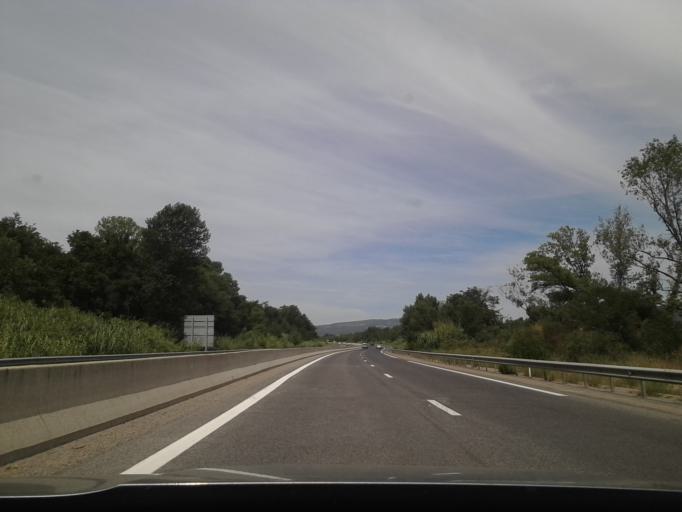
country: FR
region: Languedoc-Roussillon
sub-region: Departement des Pyrenees-Orientales
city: Corneilla-la-Riviere
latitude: 42.6868
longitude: 2.7347
